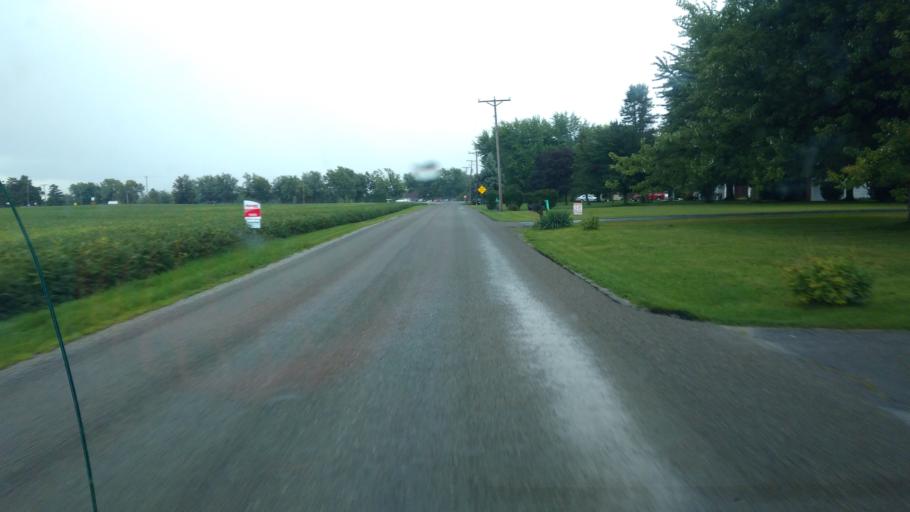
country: US
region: Ohio
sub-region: Hardin County
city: Kenton
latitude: 40.6467
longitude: -83.5762
